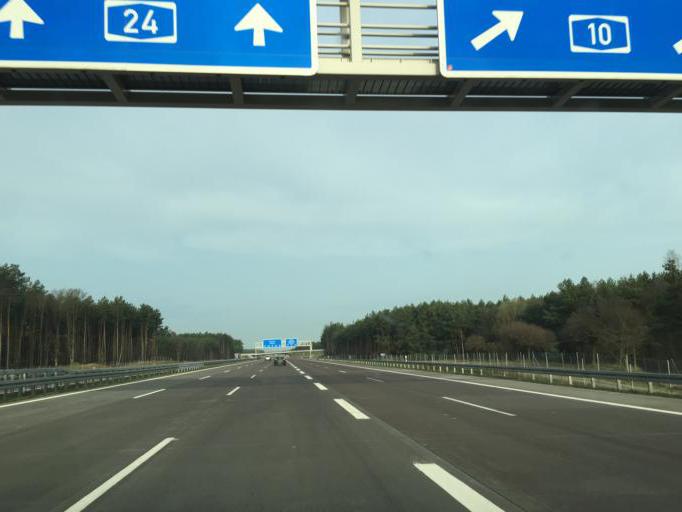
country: DE
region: Brandenburg
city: Kremmen
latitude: 52.7092
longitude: 13.0348
